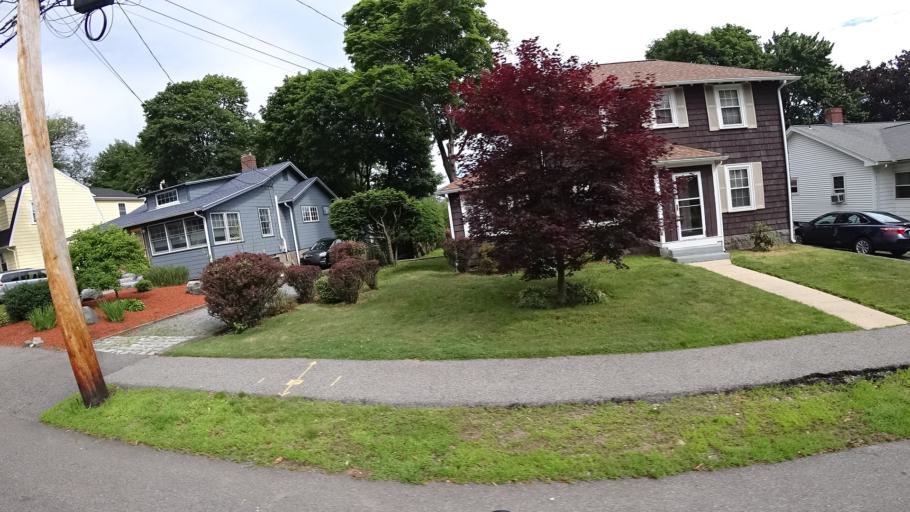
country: US
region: Massachusetts
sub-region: Norfolk County
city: Dedham
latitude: 42.2383
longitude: -71.1515
